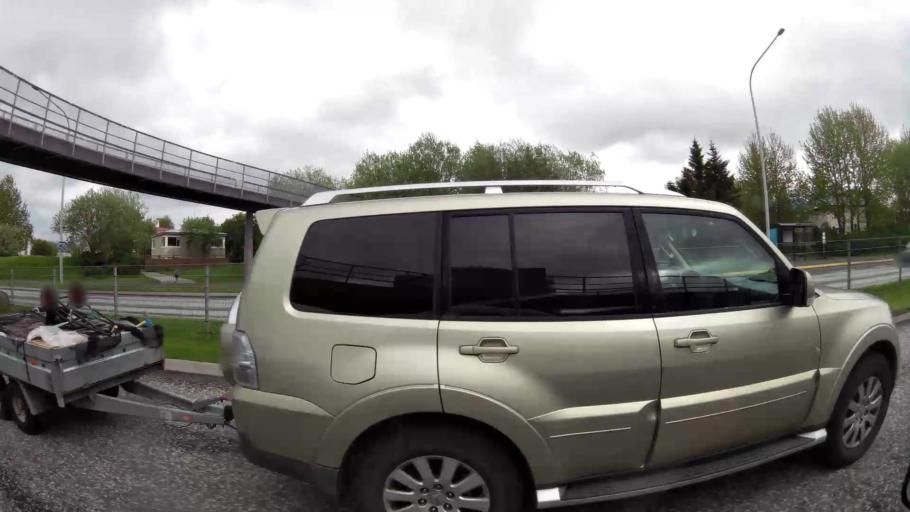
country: IS
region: Capital Region
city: Reykjavik
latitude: 64.1446
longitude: -21.8925
